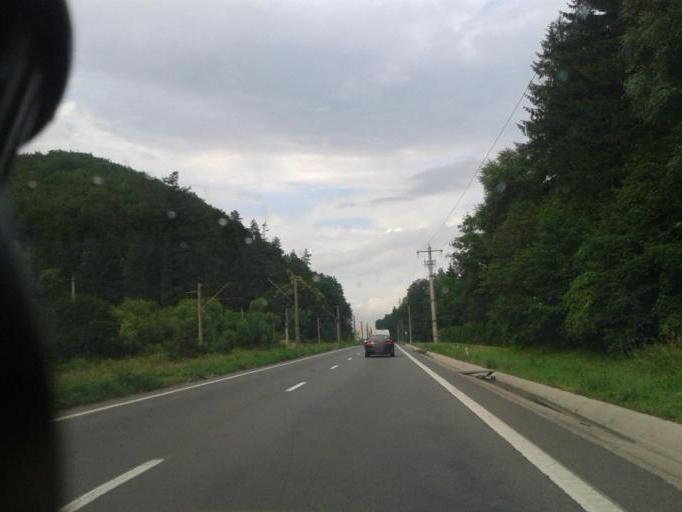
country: RO
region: Brasov
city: Brasov
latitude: 45.5979
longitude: 25.6413
